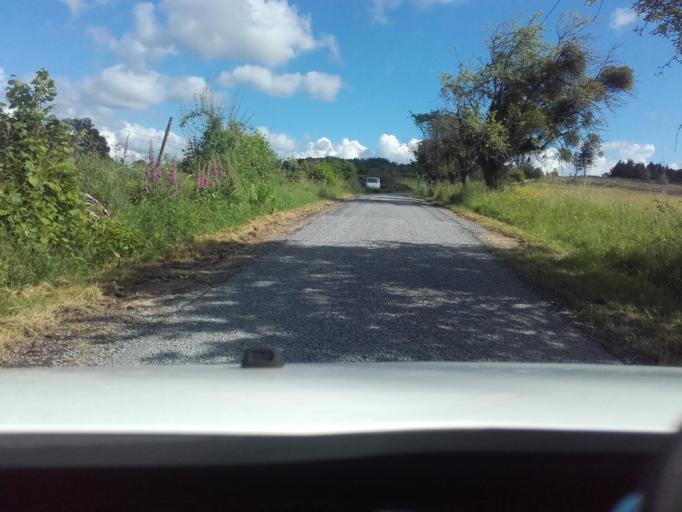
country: FR
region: Limousin
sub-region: Departement de la Correze
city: Laguenne
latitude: 45.2378
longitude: 1.8722
